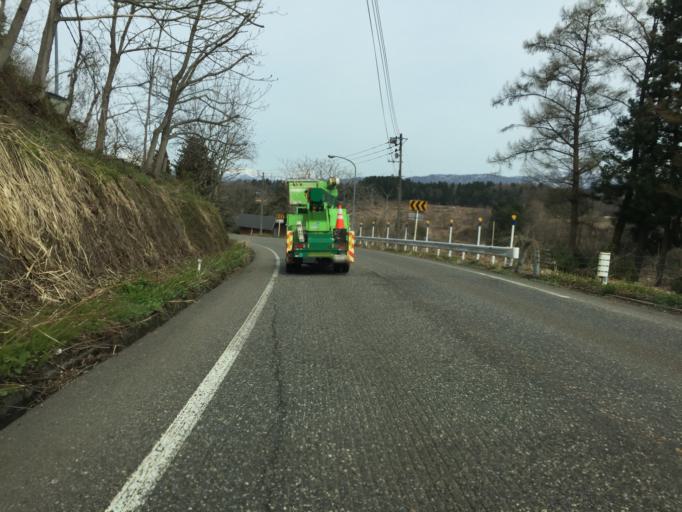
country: JP
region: Niigata
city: Tochio-honcho
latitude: 37.4526
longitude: 138.9622
